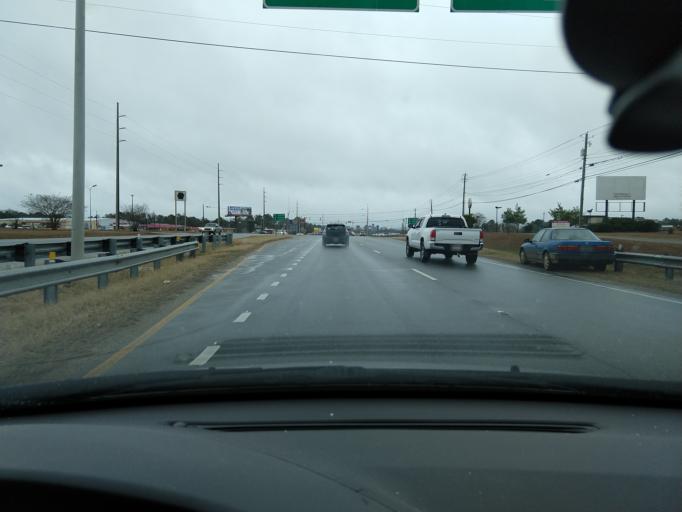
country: US
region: Alabama
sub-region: Houston County
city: Dothan
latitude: 31.2533
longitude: -85.3914
